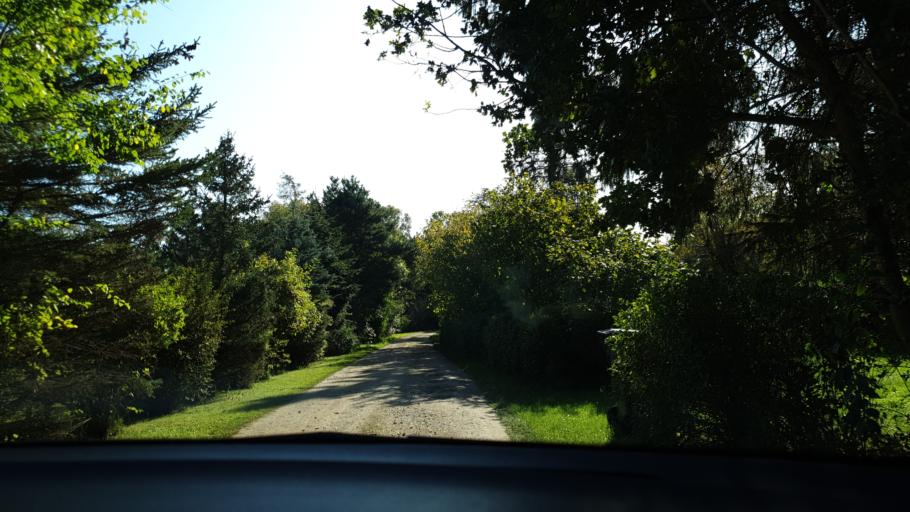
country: DK
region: Zealand
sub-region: Odsherred Kommune
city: Hojby
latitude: 55.9357
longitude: 11.6257
